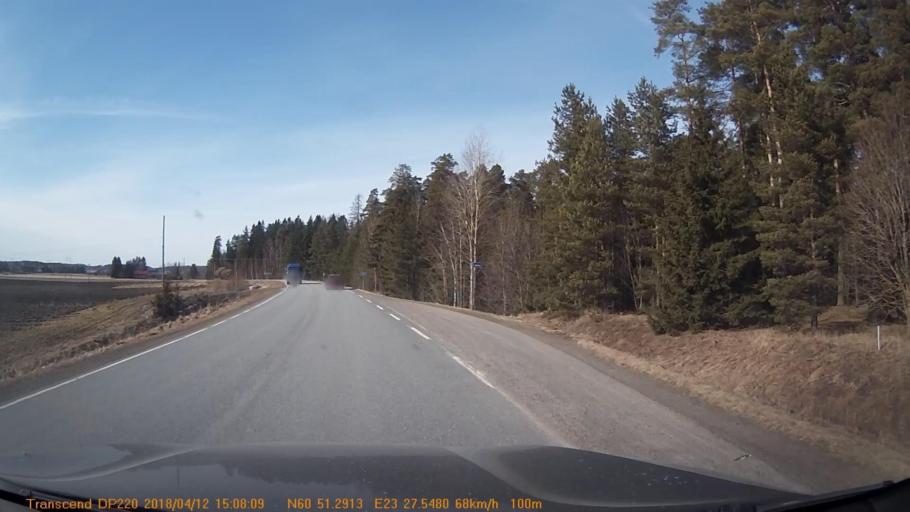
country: FI
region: Haeme
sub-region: Forssa
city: Jokioinen
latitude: 60.8552
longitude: 23.4587
